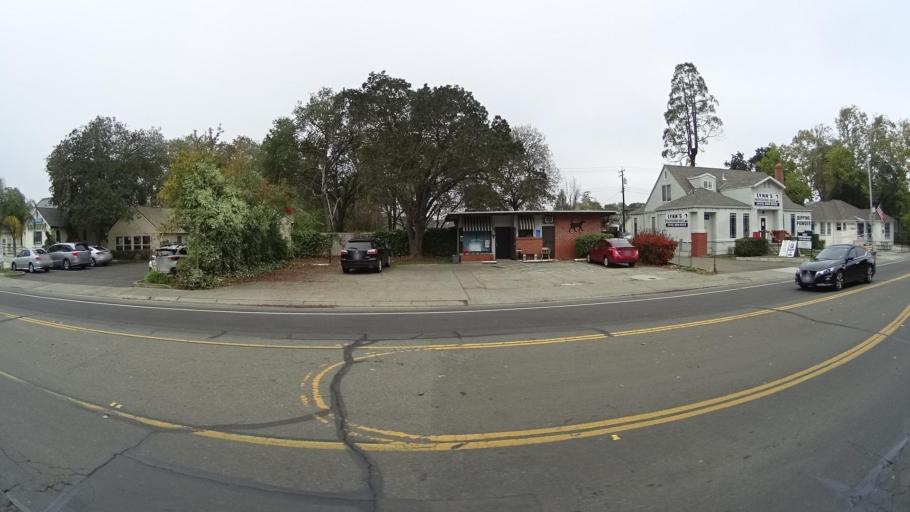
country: US
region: California
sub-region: Sacramento County
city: Elk Grove
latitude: 38.4080
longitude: -121.3719
